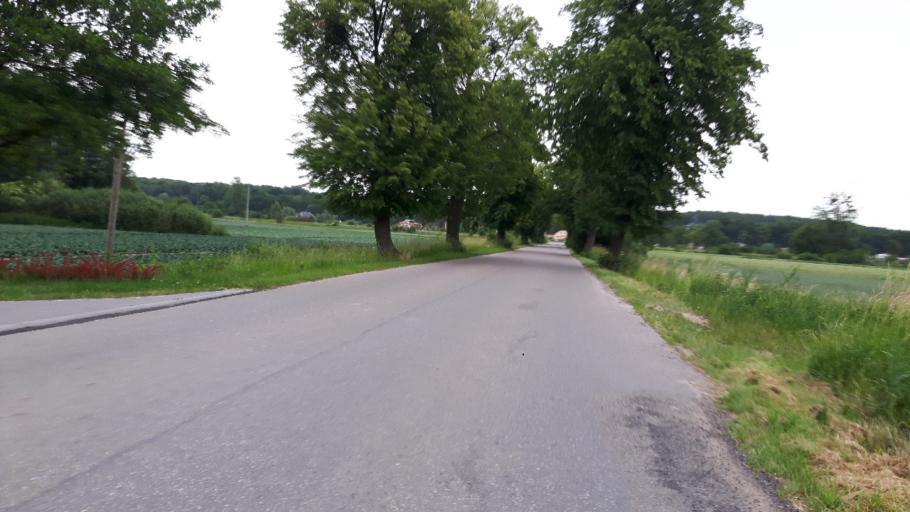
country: PL
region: Warmian-Masurian Voivodeship
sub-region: Powiat elblaski
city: Elblag
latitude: 54.2155
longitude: 19.3812
